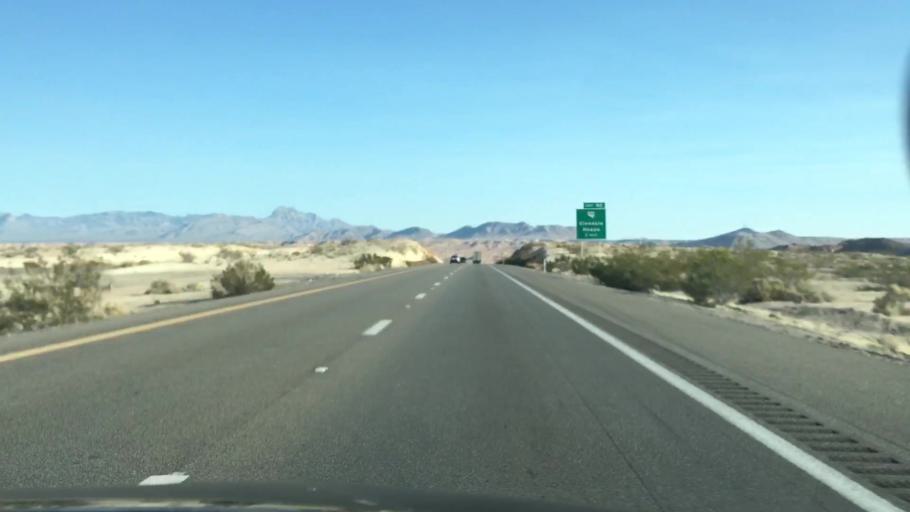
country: US
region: Nevada
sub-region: Clark County
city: Moapa Town
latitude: 36.6476
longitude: -114.5876
